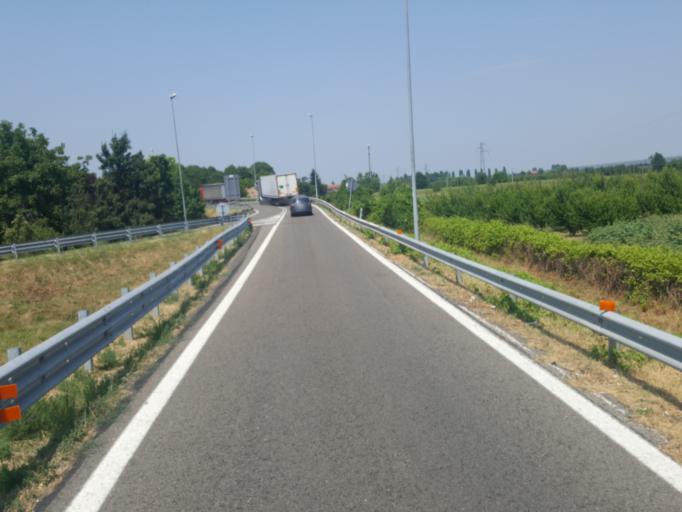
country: IT
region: Emilia-Romagna
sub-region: Provincia di Bologna
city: Calderara di Reno
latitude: 44.5275
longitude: 11.2511
